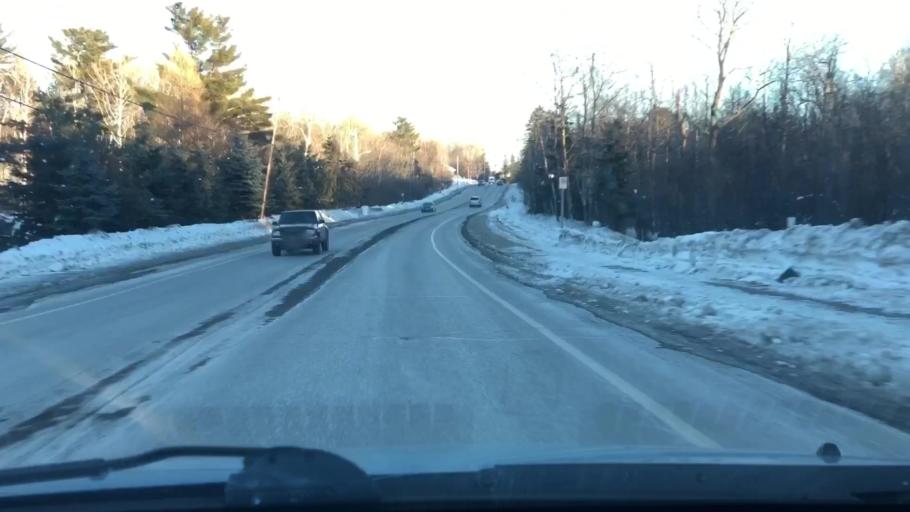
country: US
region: Minnesota
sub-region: Saint Louis County
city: Duluth
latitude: 46.8258
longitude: -92.0858
